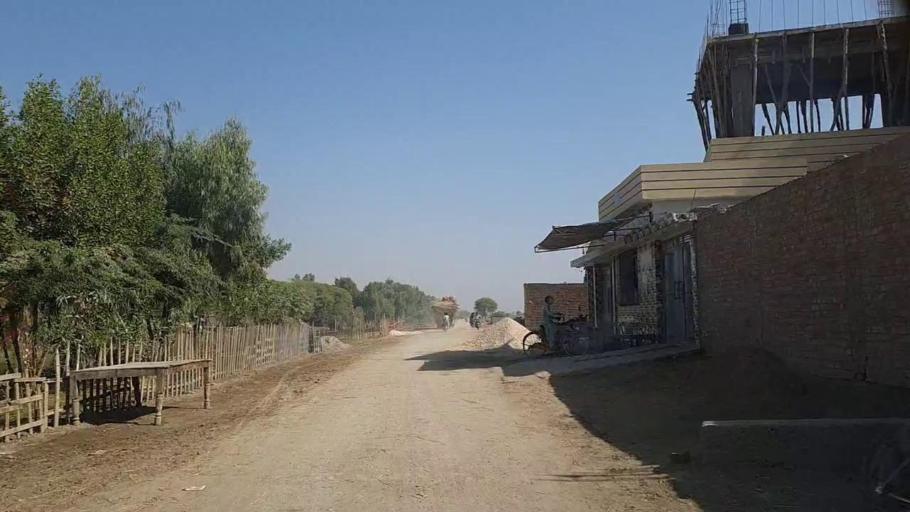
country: PK
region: Sindh
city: Thul
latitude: 28.2373
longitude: 68.7904
